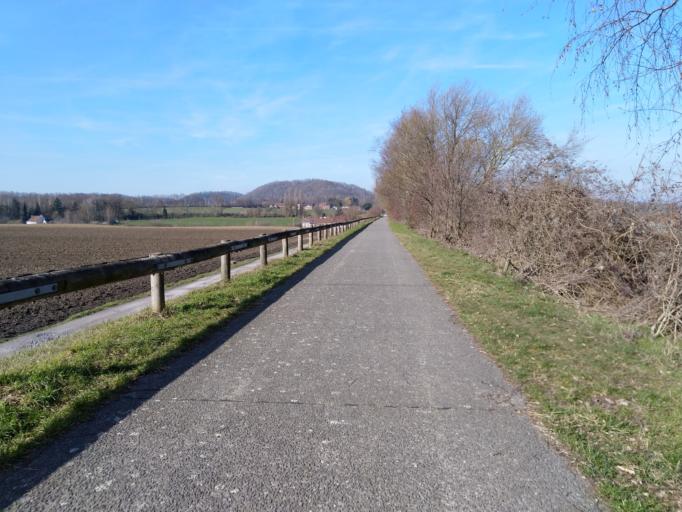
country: BE
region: Wallonia
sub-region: Province du Hainaut
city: Chasse Royale
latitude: 50.4282
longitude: 3.9190
